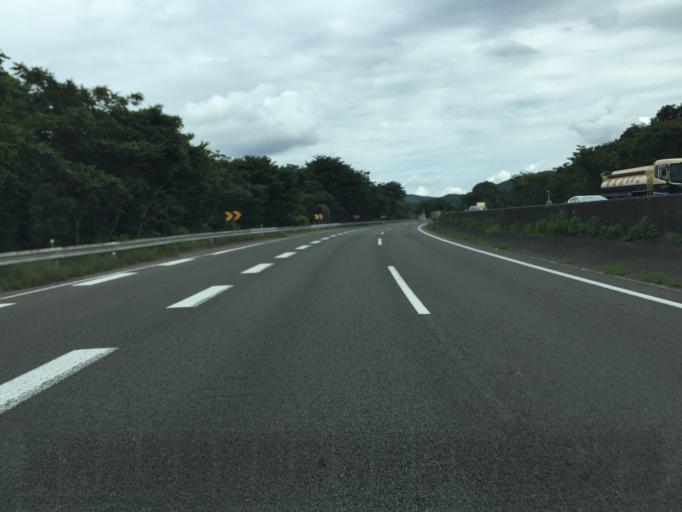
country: JP
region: Fukushima
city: Yanagawamachi-saiwaicho
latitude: 37.9108
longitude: 140.5827
